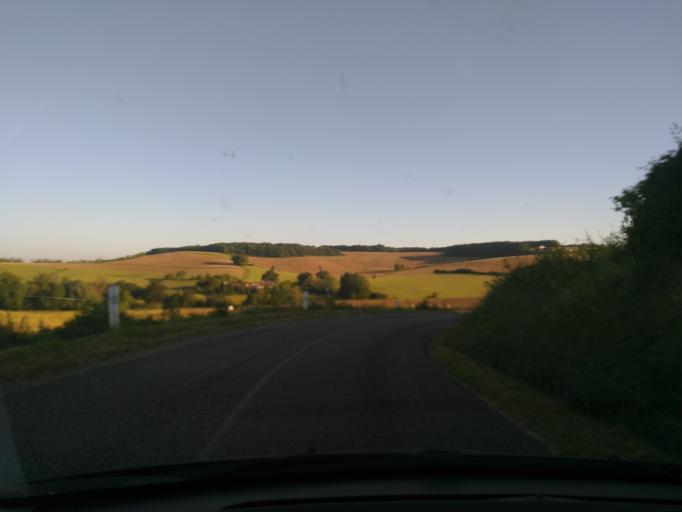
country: FR
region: Midi-Pyrenees
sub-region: Departement du Gers
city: Jegun
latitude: 43.8635
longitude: 0.5074
